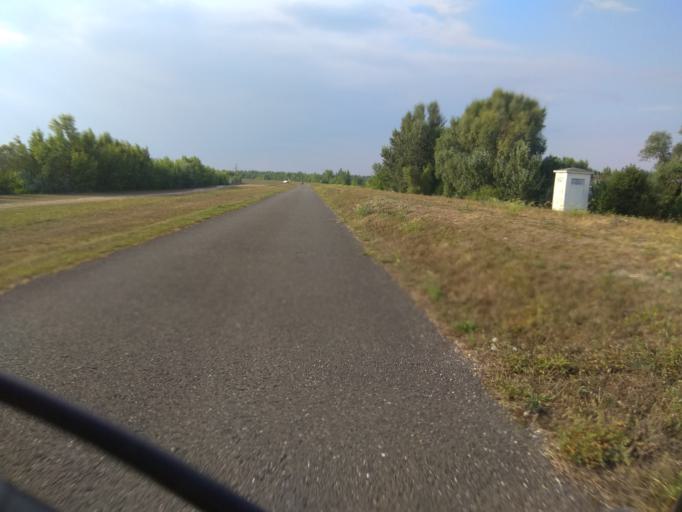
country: SK
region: Trnavsky
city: Gabcikovo
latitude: 47.8717
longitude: 17.5543
